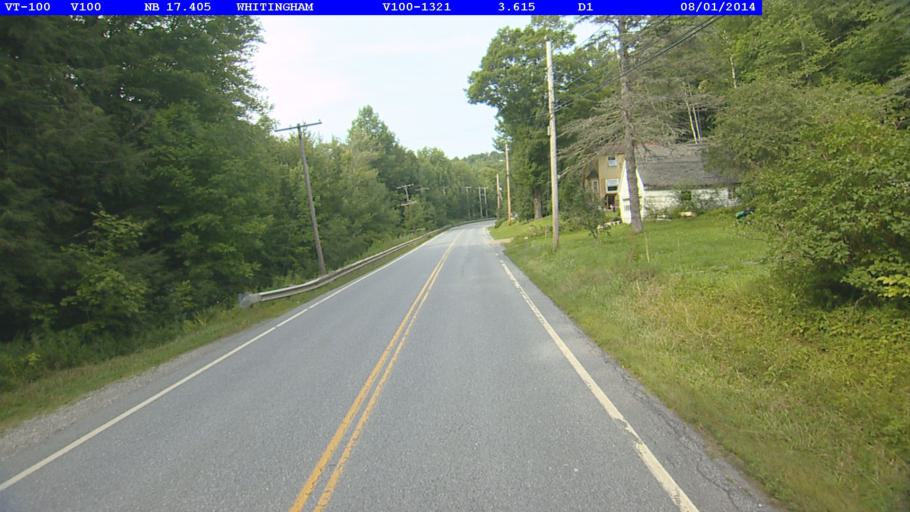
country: US
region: Massachusetts
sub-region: Franklin County
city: Charlemont
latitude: 42.7886
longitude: -72.8914
